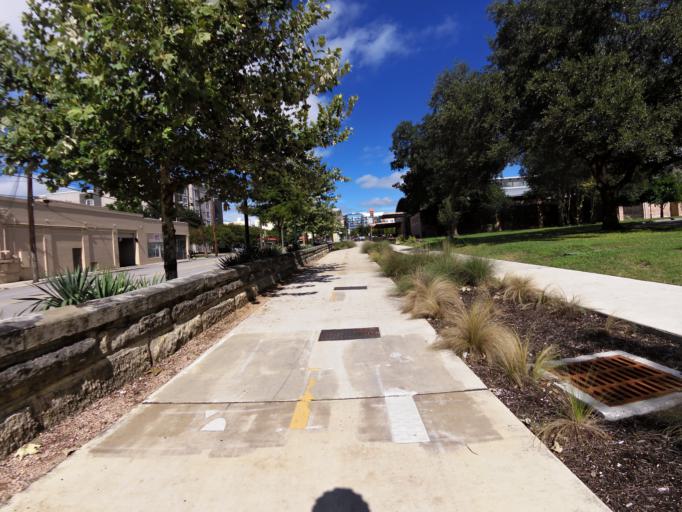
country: US
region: Texas
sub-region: Bexar County
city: San Antonio
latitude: 29.4186
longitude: -98.4970
